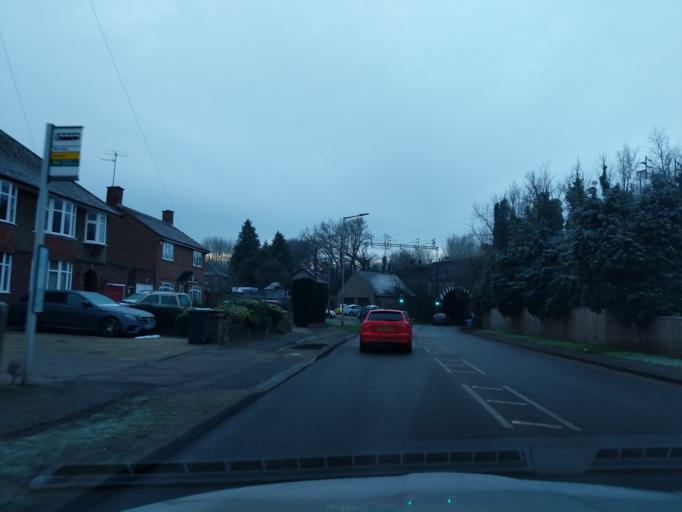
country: GB
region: England
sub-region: Hertfordshire
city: Kings Langley
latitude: 51.7241
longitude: -0.4480
